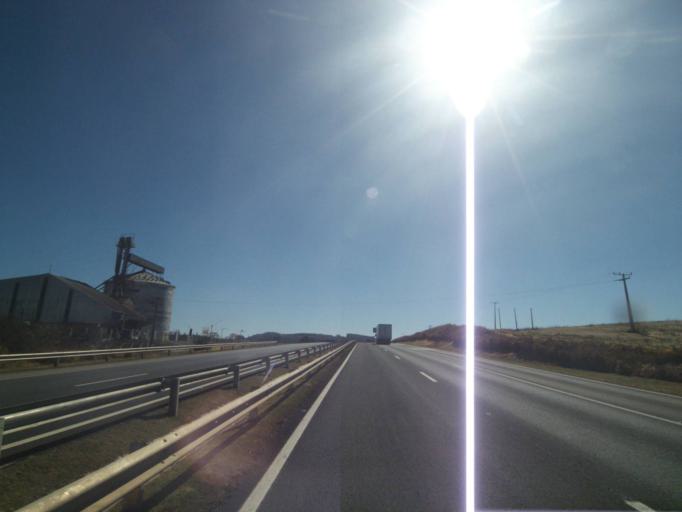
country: BR
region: Parana
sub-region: Tibagi
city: Tibagi
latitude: -24.8282
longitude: -50.4788
